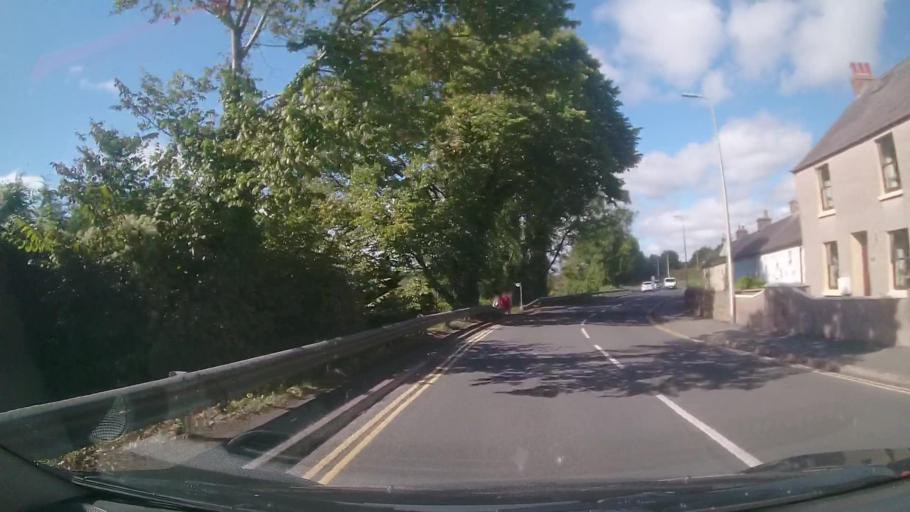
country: GB
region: Wales
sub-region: Pembrokeshire
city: Tenby
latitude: 51.6721
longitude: -4.7116
